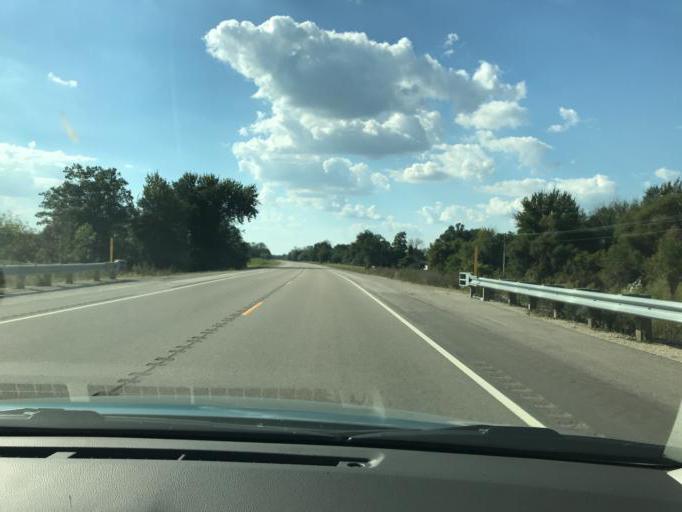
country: US
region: Wisconsin
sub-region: Green County
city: Brodhead
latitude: 42.5713
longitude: -89.3497
